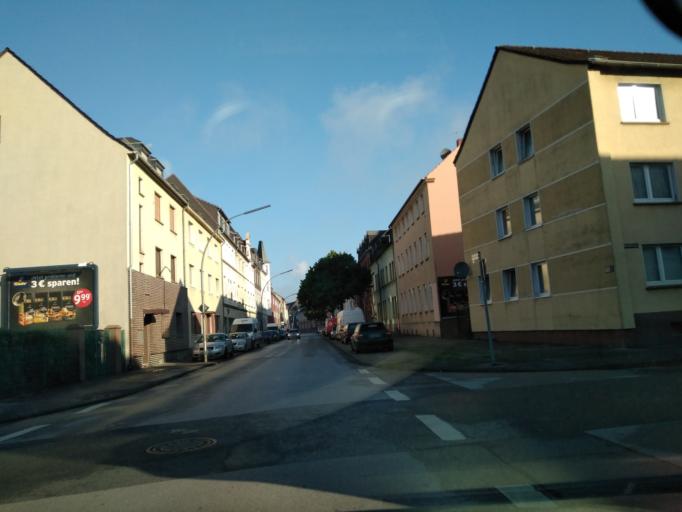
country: DE
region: North Rhine-Westphalia
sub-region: Regierungsbezirk Munster
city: Gelsenkirchen
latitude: 51.5558
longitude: 7.0905
